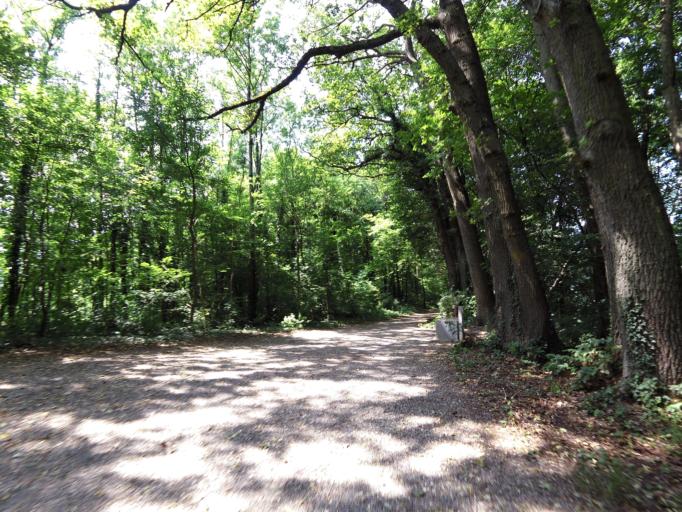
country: CH
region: Aargau
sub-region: Bezirk Baden
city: Spreitenbach
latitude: 47.4285
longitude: 8.3781
